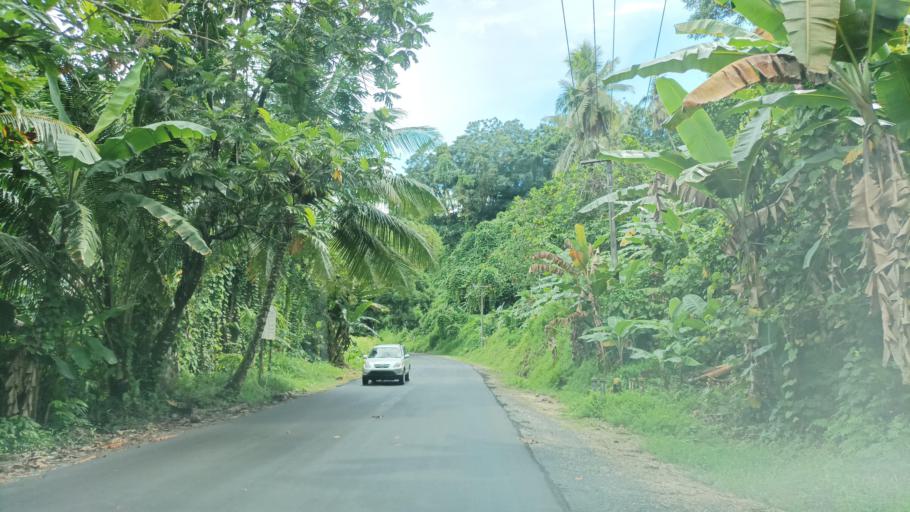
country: FM
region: Pohnpei
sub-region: Madolenihm Municipality
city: Madolenihm Municipality Government
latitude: 6.9177
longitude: 158.3062
